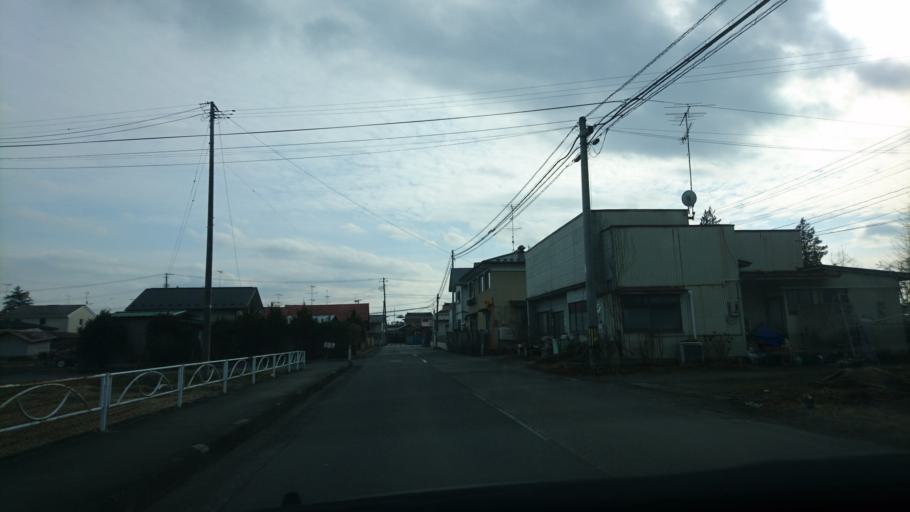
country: JP
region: Iwate
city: Ichinoseki
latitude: 38.8489
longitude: 141.1721
